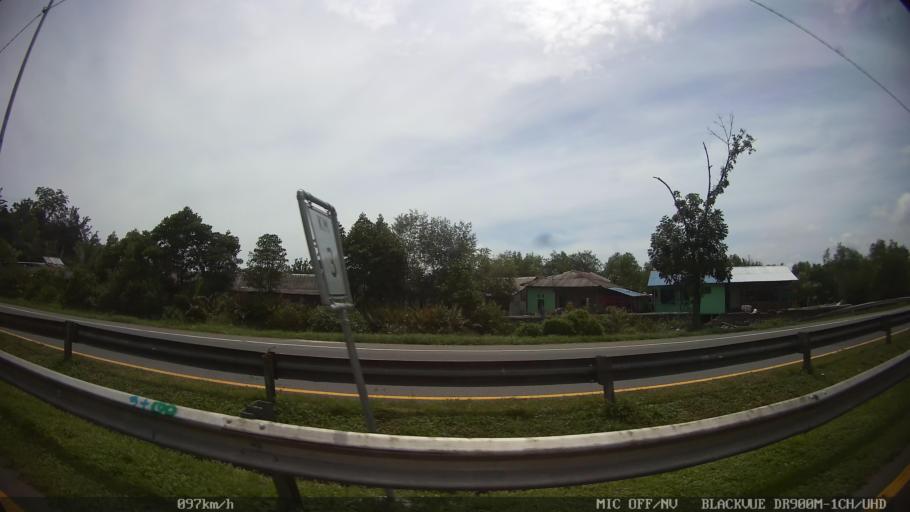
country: ID
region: North Sumatra
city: Labuhan Deli
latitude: 3.7405
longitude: 98.6794
